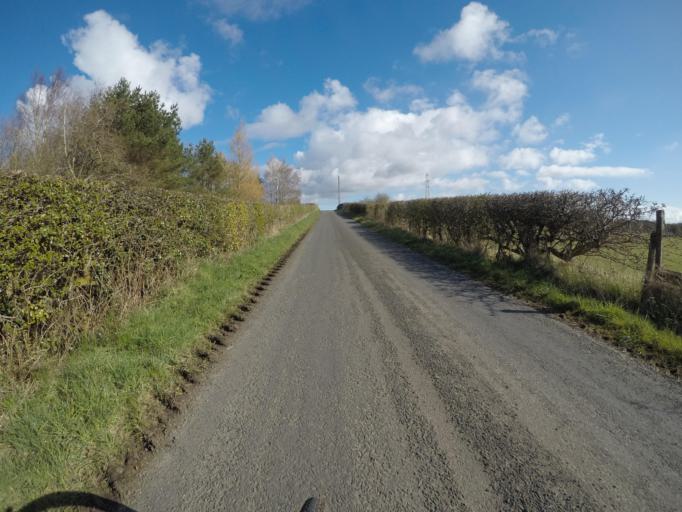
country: GB
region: Scotland
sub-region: North Ayrshire
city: Irvine
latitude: 55.6584
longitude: -4.6544
